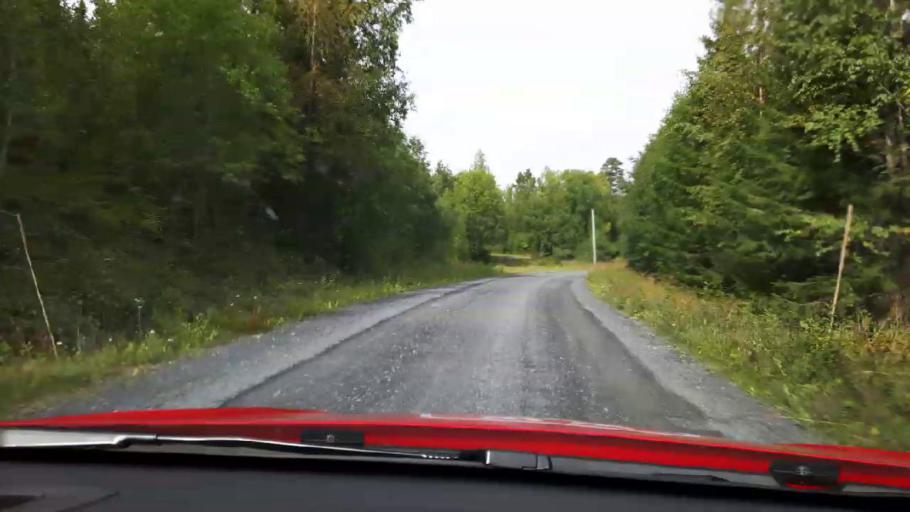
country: SE
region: Jaemtland
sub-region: Are Kommun
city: Jarpen
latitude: 63.2778
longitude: 13.7337
